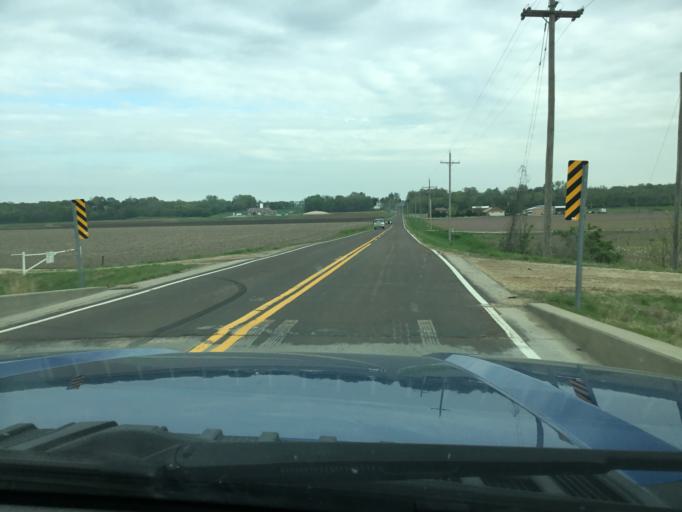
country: US
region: Kansas
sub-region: Shawnee County
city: Topeka
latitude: 39.0981
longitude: -95.7483
